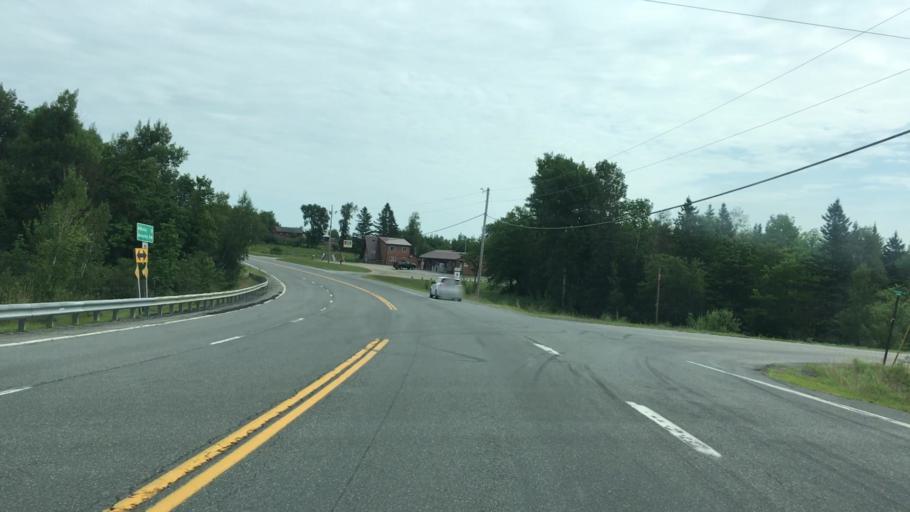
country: US
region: Maine
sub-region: Washington County
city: Calais
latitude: 45.0936
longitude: -67.4702
